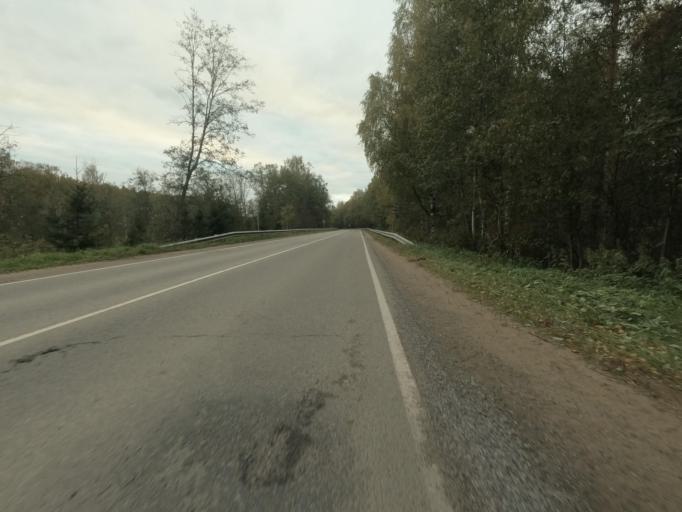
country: RU
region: Leningrad
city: Pavlovo
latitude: 59.7911
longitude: 30.9602
